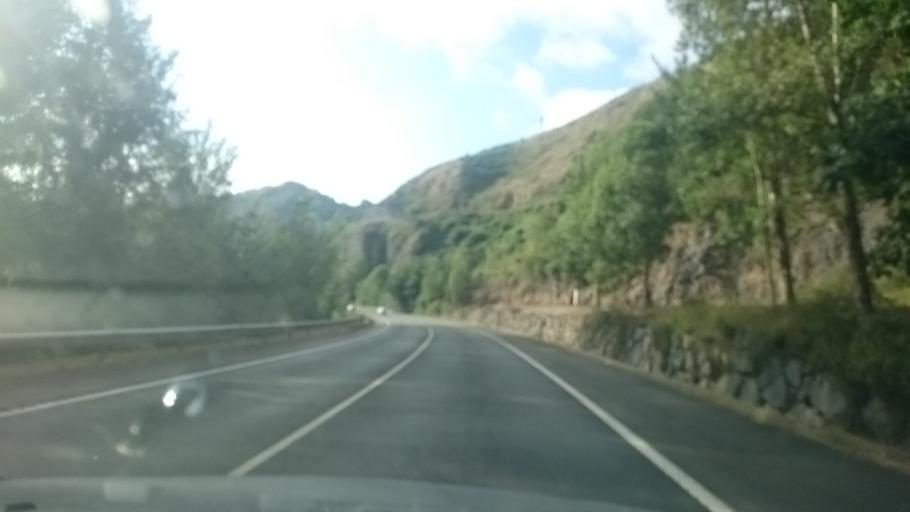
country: ES
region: Asturias
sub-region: Province of Asturias
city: Sama
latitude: 43.3302
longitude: -5.7490
